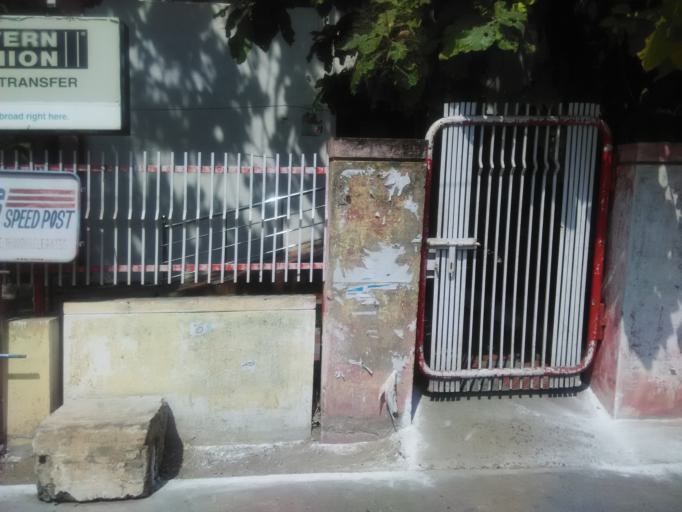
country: IN
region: Andhra Pradesh
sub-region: Prakasam
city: Chirala
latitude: 15.8314
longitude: 80.3521
